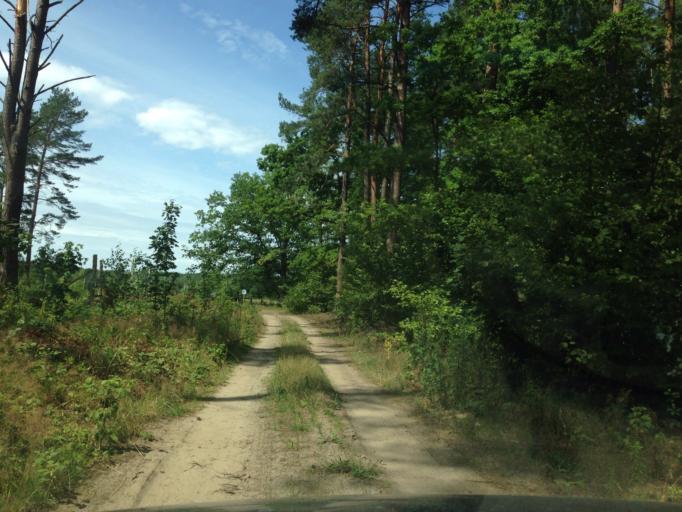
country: PL
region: Kujawsko-Pomorskie
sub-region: Powiat brodnicki
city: Bartniczka
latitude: 53.2813
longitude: 19.5666
